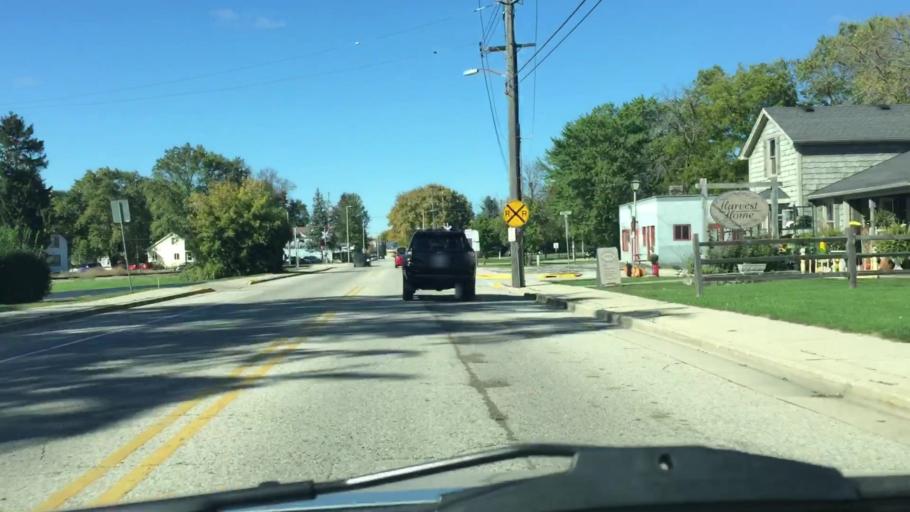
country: US
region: Wisconsin
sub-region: Waukesha County
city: Pewaukee
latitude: 43.0832
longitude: -88.2556
